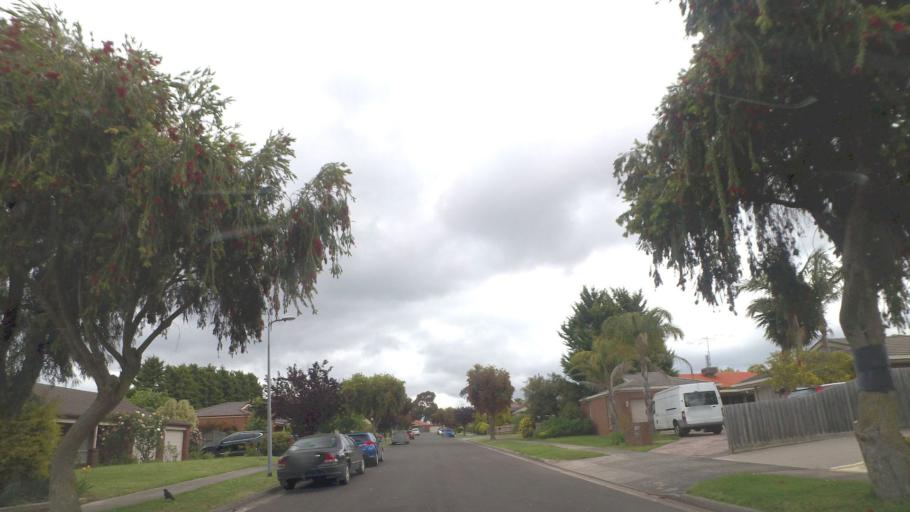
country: AU
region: Victoria
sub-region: Maroondah
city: Heathmont
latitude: -37.8438
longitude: 145.2539
